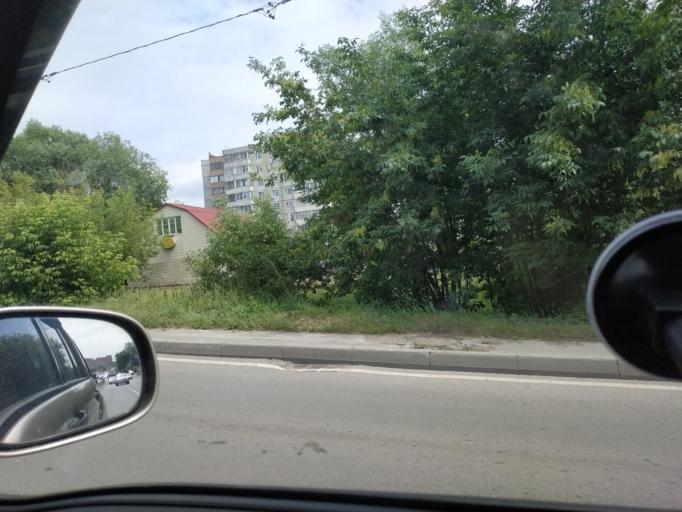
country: RU
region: Moskovskaya
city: Shchelkovo
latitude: 55.9268
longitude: 38.0011
